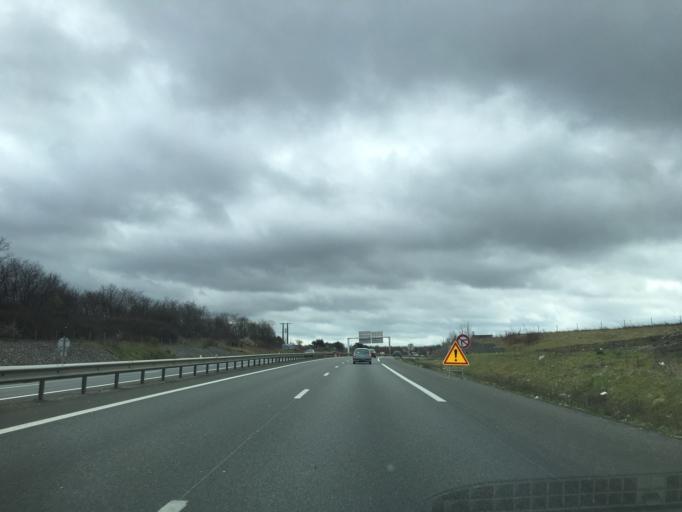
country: FR
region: Ile-de-France
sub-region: Departement de Seine-et-Marne
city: Brie-Comte-Robert
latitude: 48.6538
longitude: 2.6160
